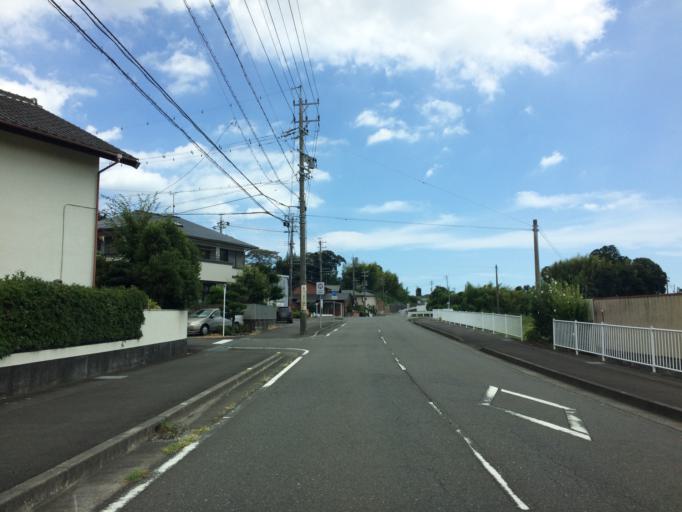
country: JP
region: Shizuoka
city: Yaizu
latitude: 34.8989
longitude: 138.2989
